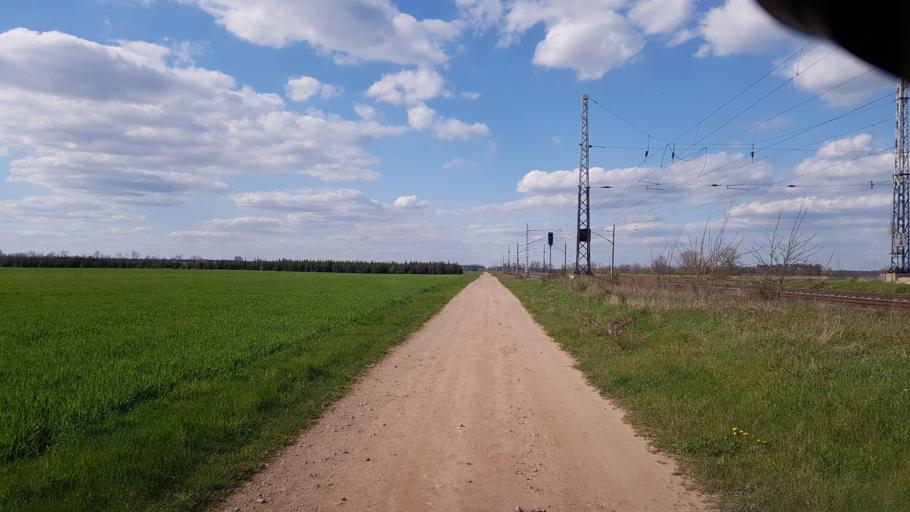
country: DE
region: Brandenburg
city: Muhlberg
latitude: 51.5032
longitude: 13.2794
